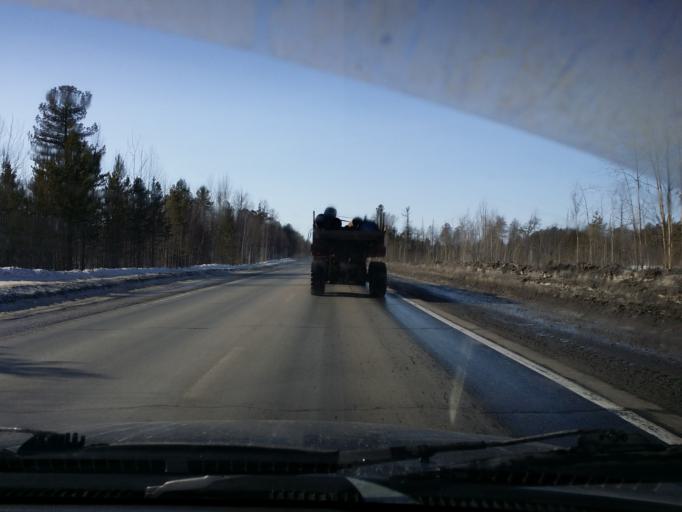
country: RU
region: Khanty-Mansiyskiy Avtonomnyy Okrug
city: Megion
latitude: 61.1622
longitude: 75.7037
